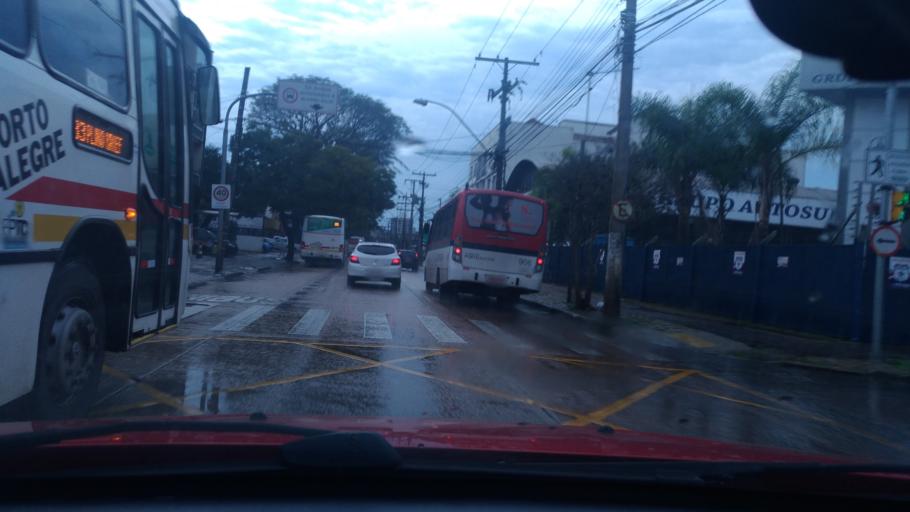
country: BR
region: Rio Grande do Sul
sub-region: Porto Alegre
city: Porto Alegre
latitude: -30.0056
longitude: -51.1996
